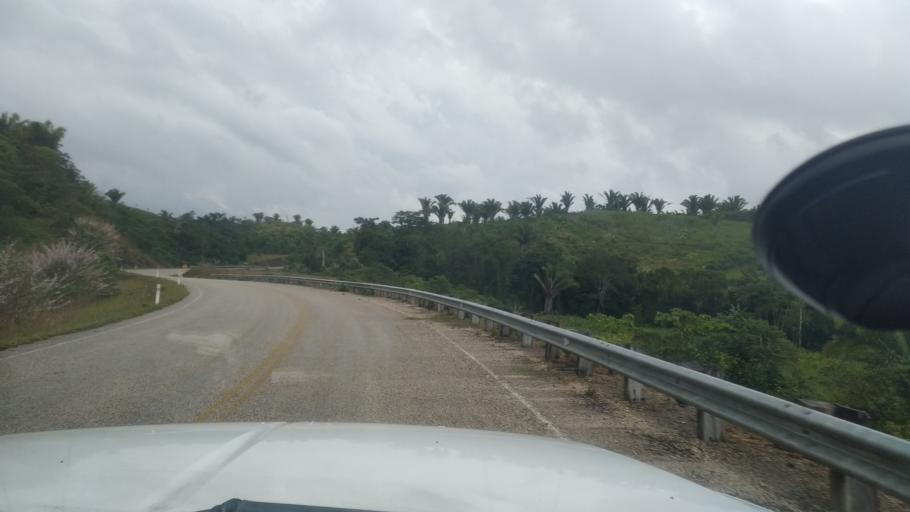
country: GT
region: Peten
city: San Luis
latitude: 16.1910
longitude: -89.1715
